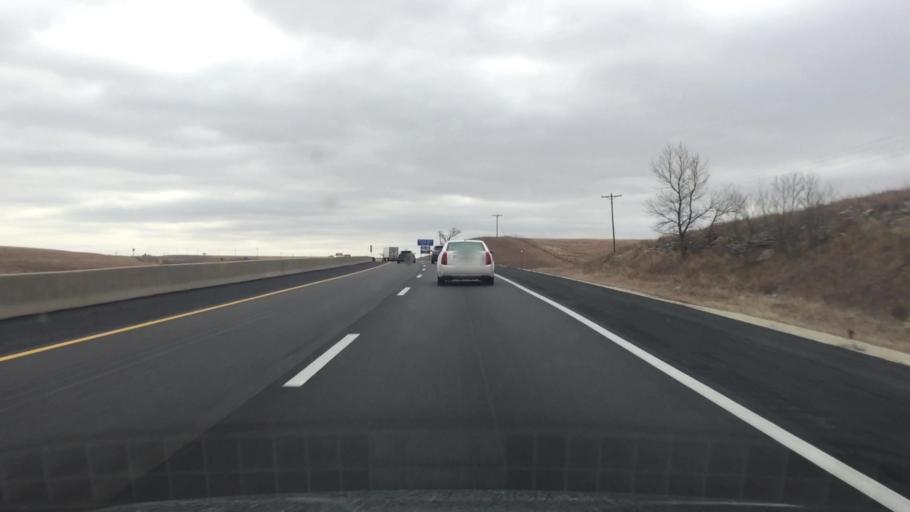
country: US
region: Kansas
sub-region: Chase County
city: Cottonwood Falls
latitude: 38.1151
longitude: -96.5696
